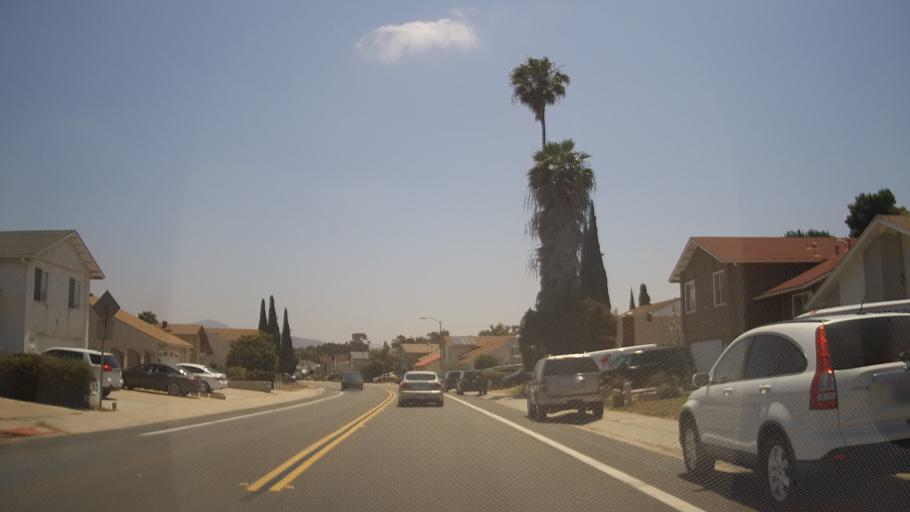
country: US
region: California
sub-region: San Diego County
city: Bonita
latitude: 32.6667
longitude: -117.0568
